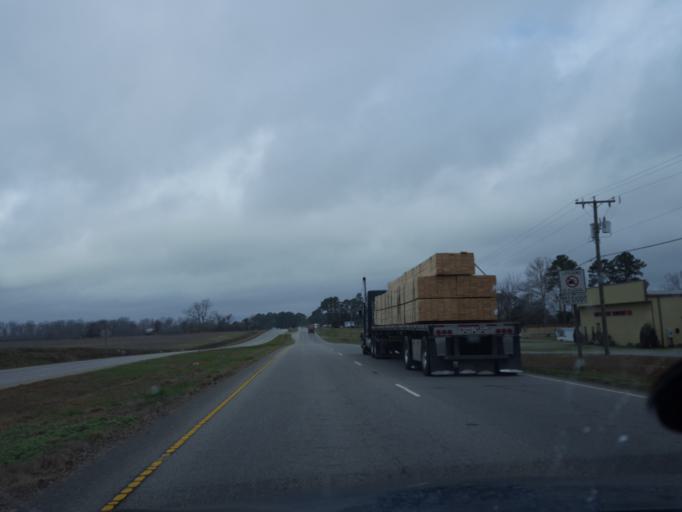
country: US
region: North Carolina
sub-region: Washington County
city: Plymouth
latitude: 35.8294
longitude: -76.7892
